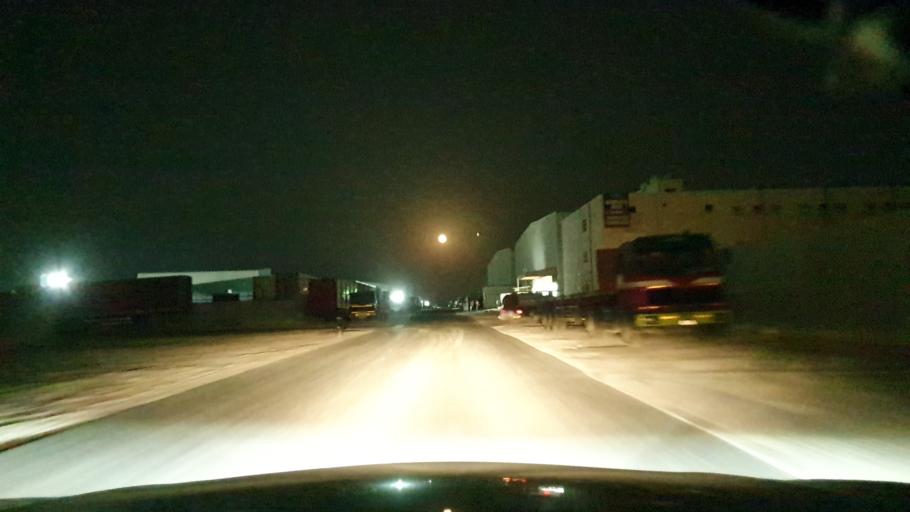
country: BH
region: Northern
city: Sitrah
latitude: 26.0973
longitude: 50.6186
